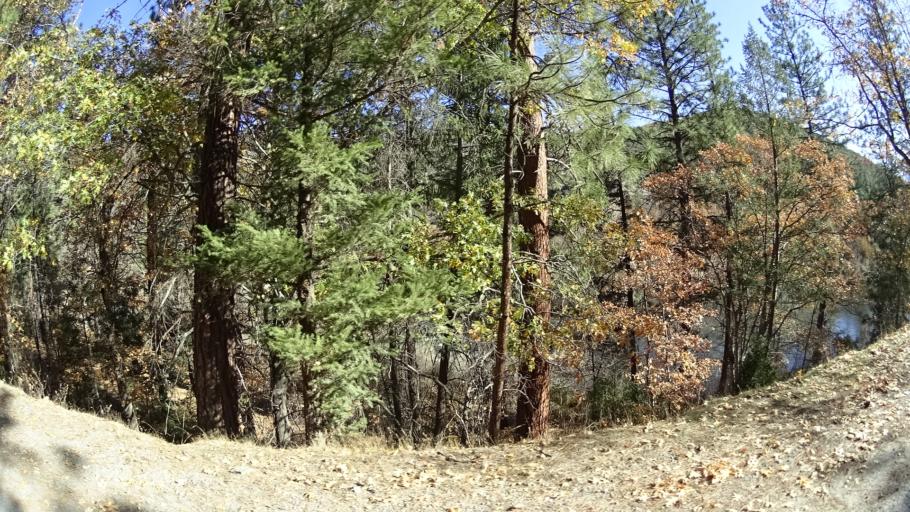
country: US
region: California
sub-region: Siskiyou County
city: Yreka
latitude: 41.8596
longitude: -122.7060
